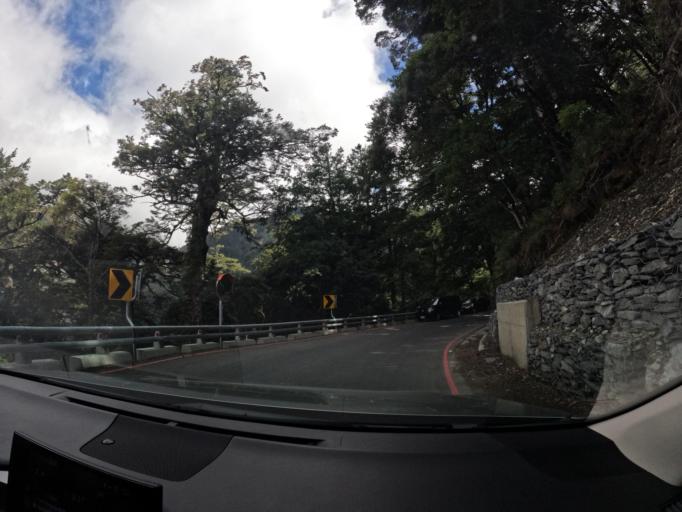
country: TW
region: Taiwan
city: Yujing
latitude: 23.2668
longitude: 120.9393
